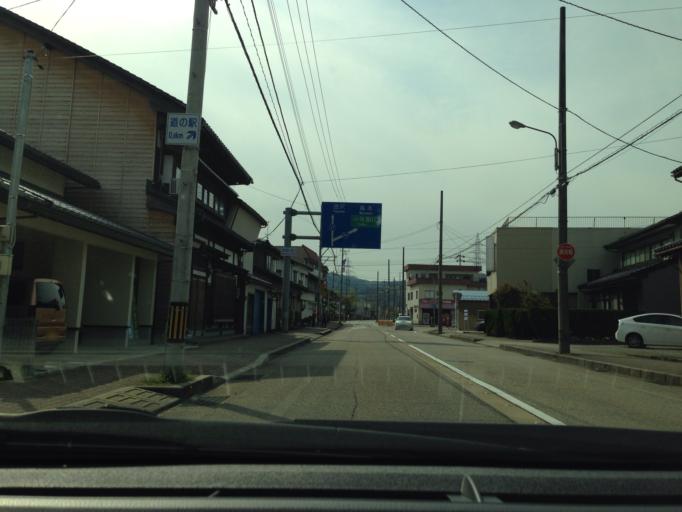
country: JP
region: Toyama
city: Fukumitsu
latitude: 36.5615
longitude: 136.8682
